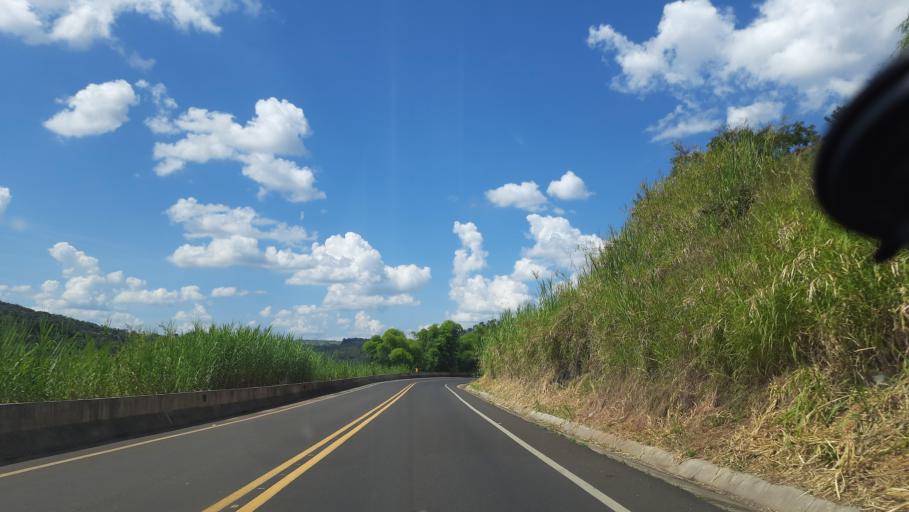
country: BR
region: Sao Paulo
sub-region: Sao Jose Do Rio Pardo
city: Sao Jose do Rio Pardo
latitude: -21.6038
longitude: -46.9421
